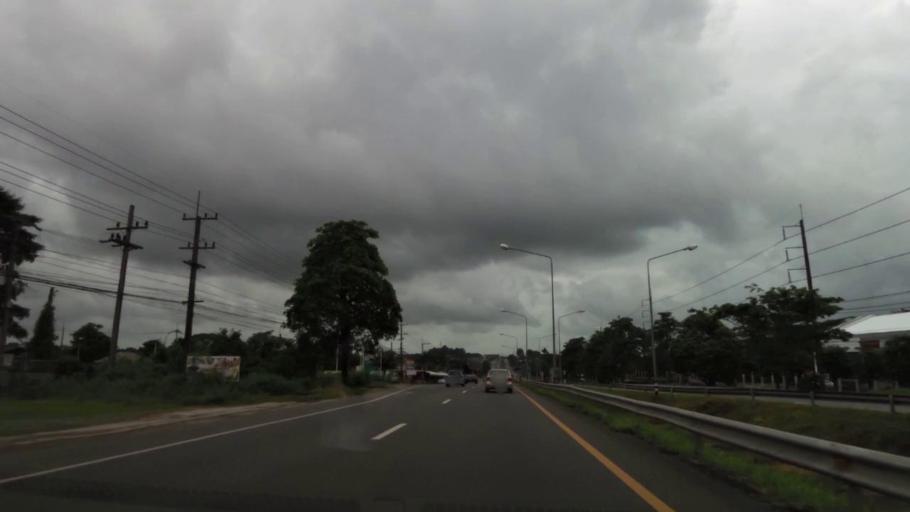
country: TH
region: Chanthaburi
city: Tha Mai
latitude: 12.6550
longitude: 102.0526
